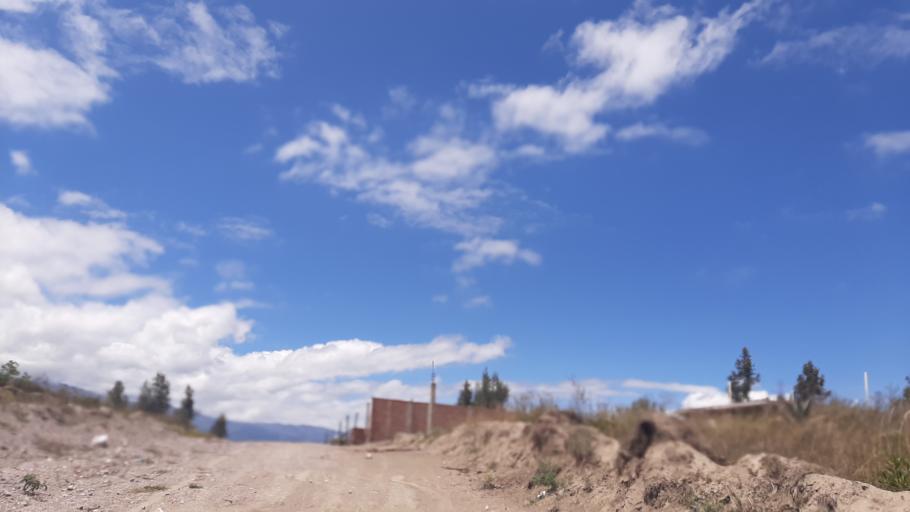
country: EC
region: Chimborazo
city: Riobamba
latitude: -1.6506
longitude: -78.6352
